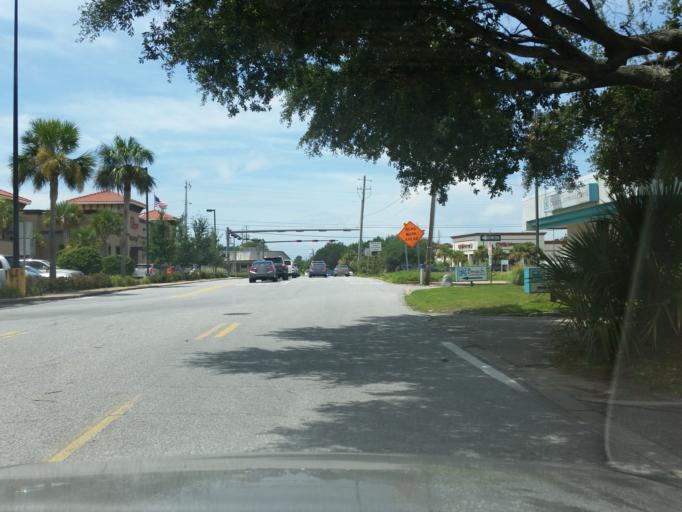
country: US
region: Florida
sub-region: Santa Rosa County
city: Gulf Breeze
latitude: 30.3662
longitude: -87.1691
